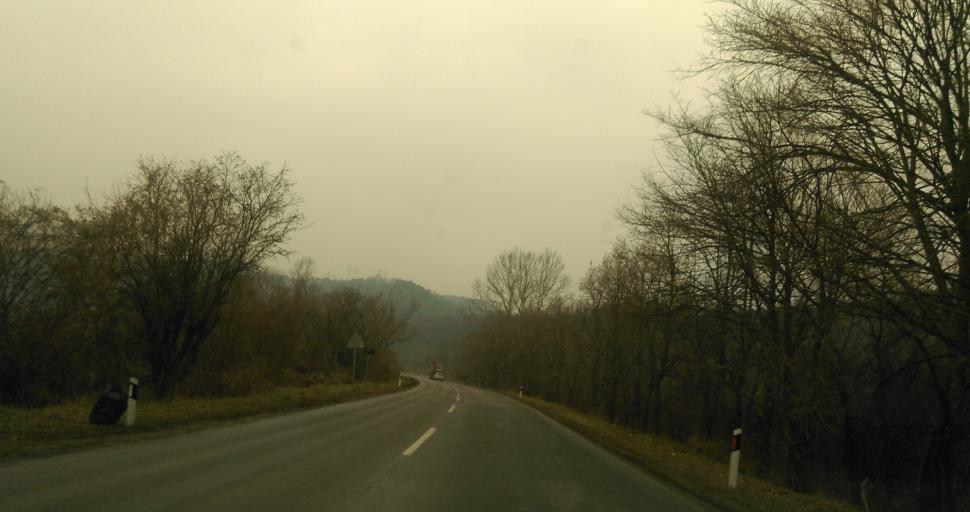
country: RS
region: Central Serbia
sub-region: Belgrade
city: Zvezdara
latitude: 44.7340
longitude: 20.5531
